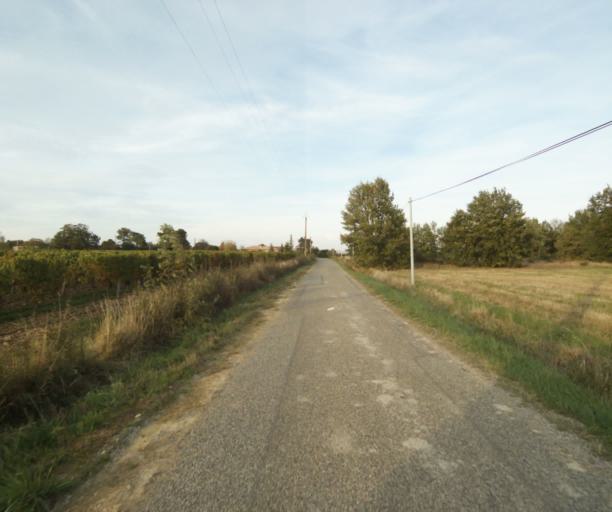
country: FR
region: Midi-Pyrenees
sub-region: Departement du Tarn-et-Garonne
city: Campsas
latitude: 43.8692
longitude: 1.3363
